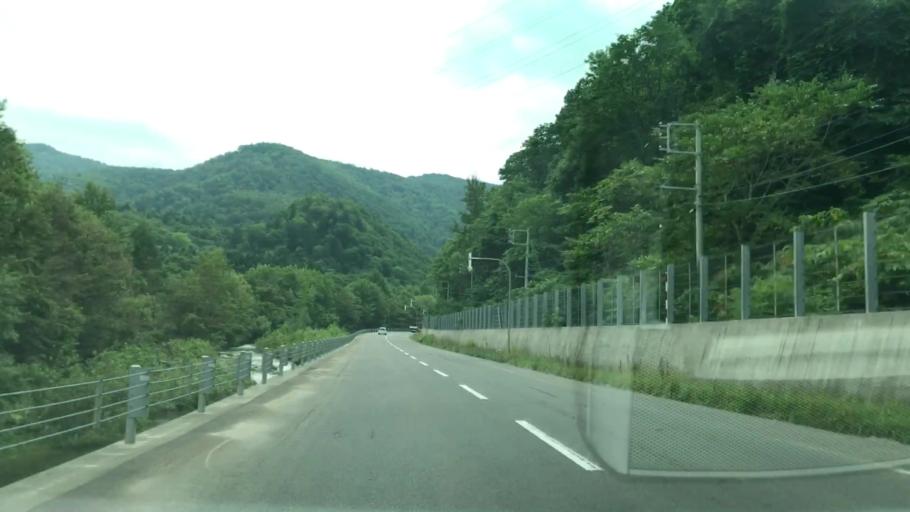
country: JP
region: Hokkaido
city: Yoichi
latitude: 43.0382
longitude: 140.8605
